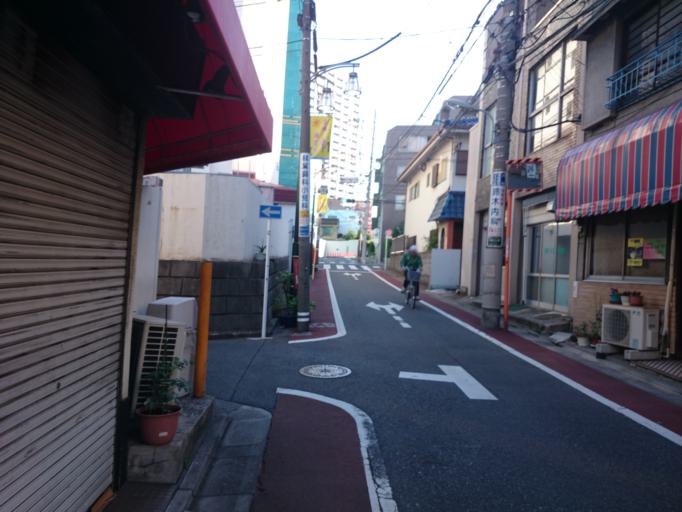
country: JP
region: Kanagawa
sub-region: Kawasaki-shi
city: Kawasaki
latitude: 35.6048
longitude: 139.7376
